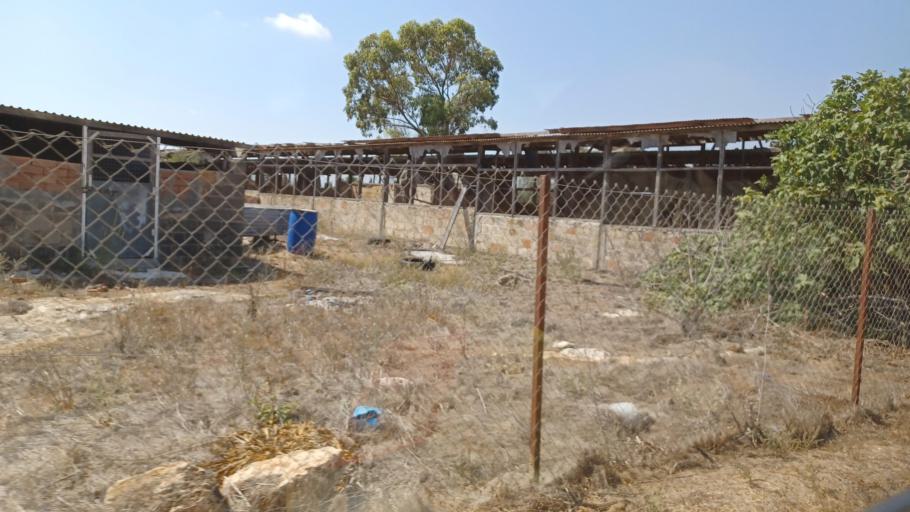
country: CY
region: Ammochostos
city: Frenaros
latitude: 35.0666
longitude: 33.9066
